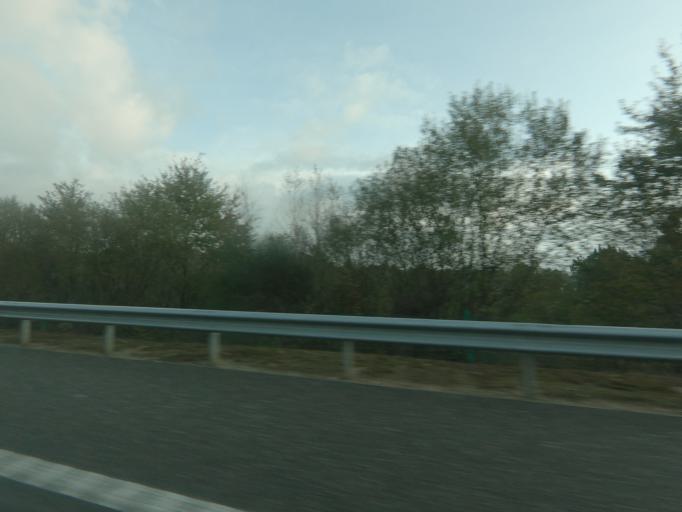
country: ES
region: Galicia
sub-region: Provincia de Pontevedra
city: Tui
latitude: 42.1044
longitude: -8.6462
